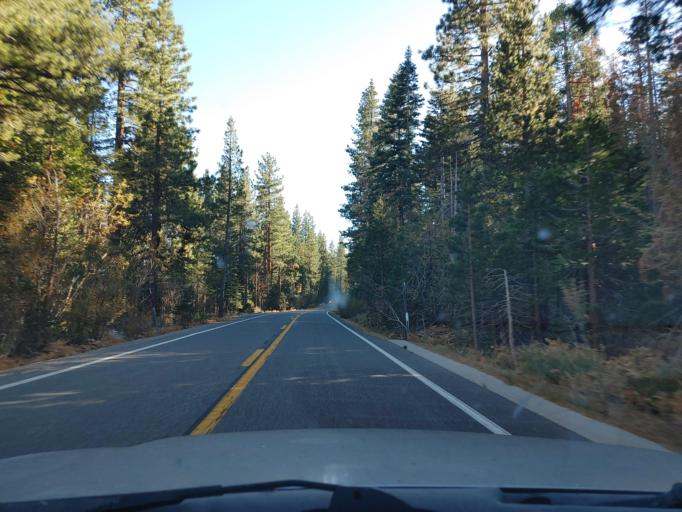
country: US
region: California
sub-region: Placer County
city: Tahoma
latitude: 38.9688
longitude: -120.0977
